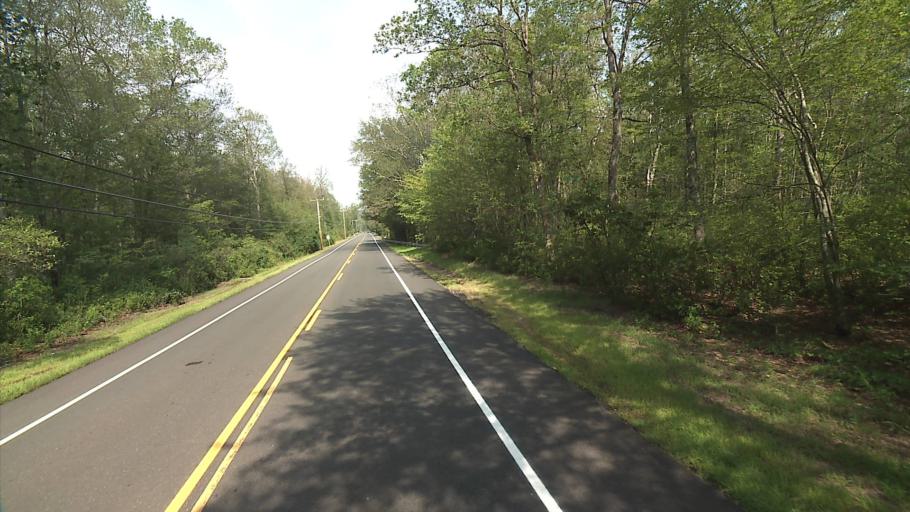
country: US
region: Connecticut
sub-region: Middlesex County
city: Durham
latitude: 41.3917
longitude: -72.6491
